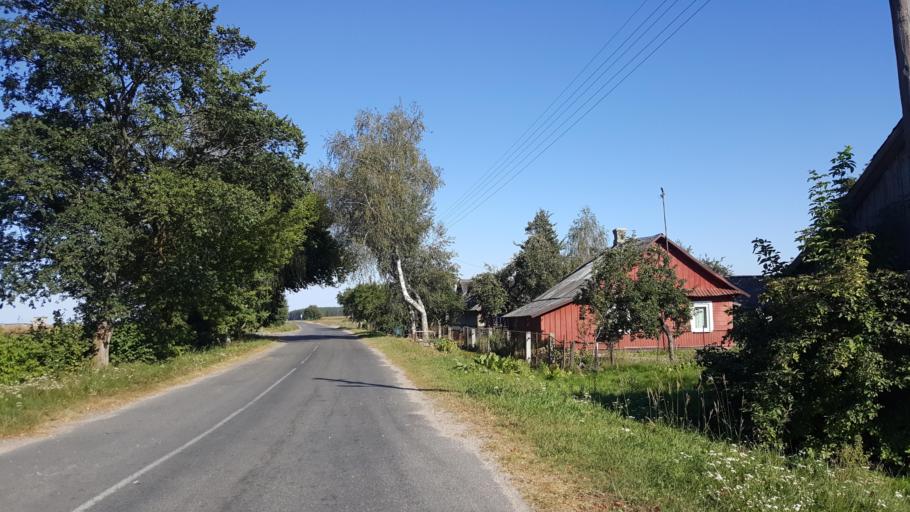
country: PL
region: Lublin Voivodeship
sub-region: Powiat bialski
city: Janow Podlaski
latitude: 52.2401
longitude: 23.2445
